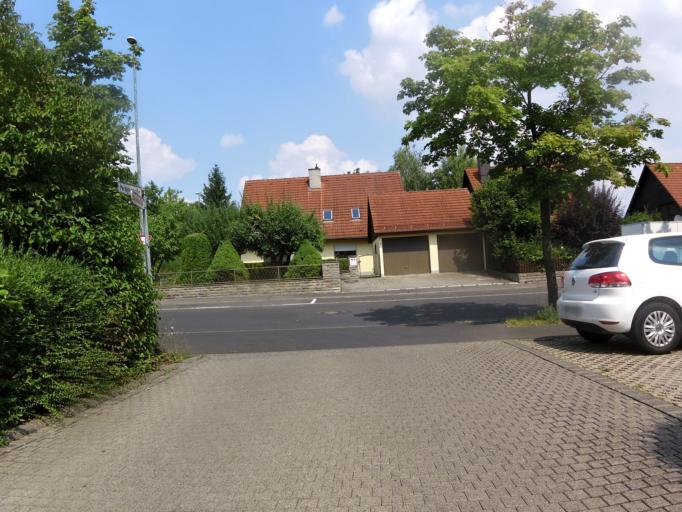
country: DE
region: Bavaria
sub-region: Regierungsbezirk Unterfranken
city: Randersacker
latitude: 49.7433
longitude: 9.9611
